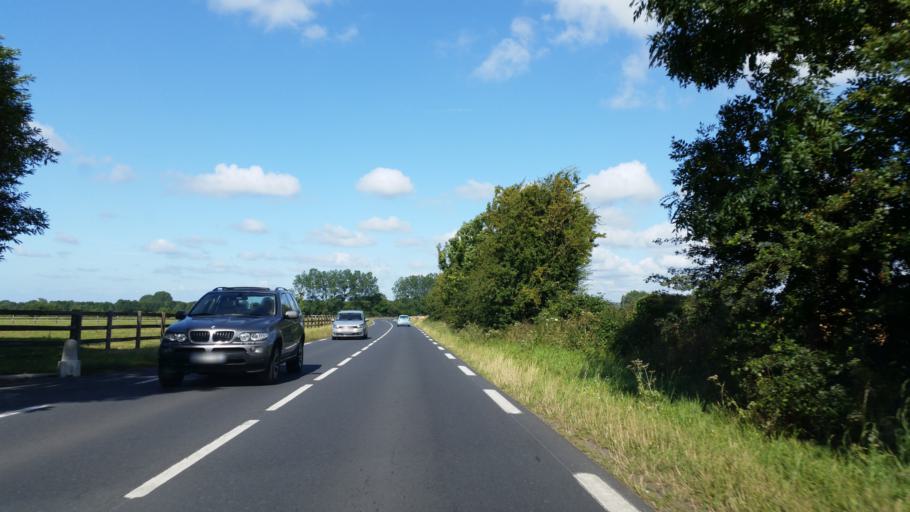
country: FR
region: Lower Normandy
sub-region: Departement du Calvados
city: Bavent
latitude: 49.2473
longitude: -0.1788
